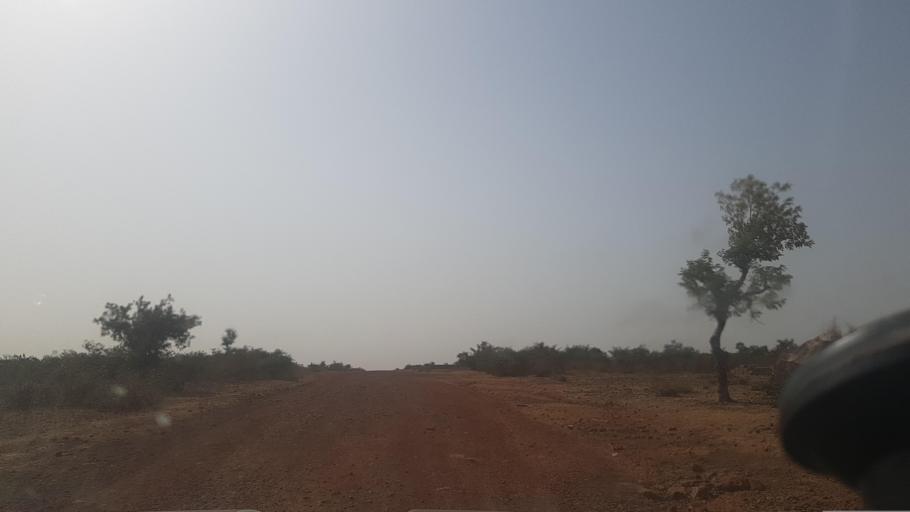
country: ML
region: Segou
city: Baroueli
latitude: 13.1599
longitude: -6.5174
